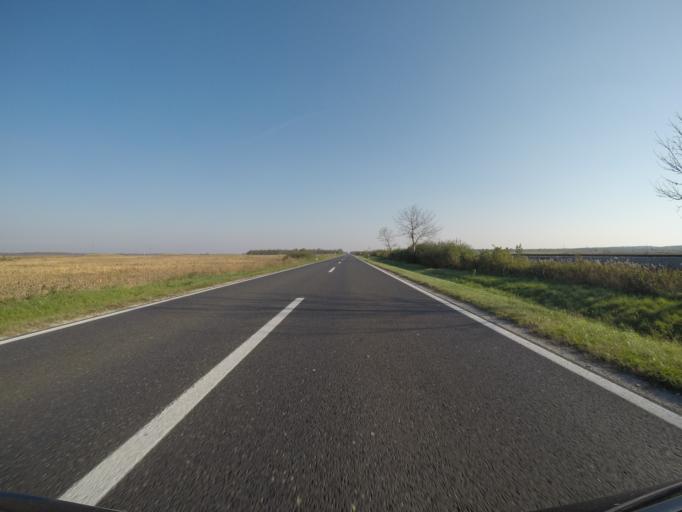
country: HR
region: Koprivnicko-Krizevacka
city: Kalinovac
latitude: 46.0100
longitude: 17.1006
